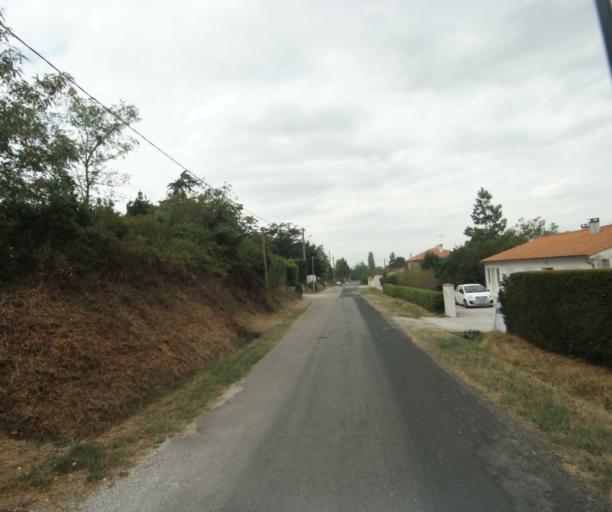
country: FR
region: Midi-Pyrenees
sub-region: Departement de la Haute-Garonne
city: Revel
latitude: 43.4483
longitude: 2.0040
